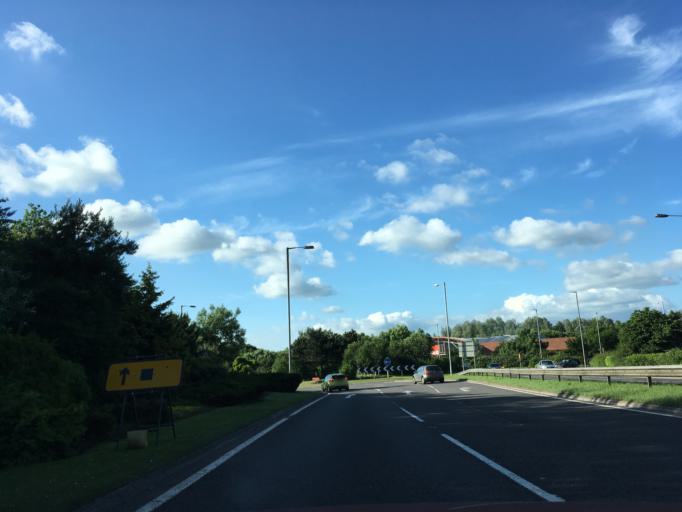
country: GB
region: England
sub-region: Somerset
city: Creech Saint Michael
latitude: 51.0212
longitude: -3.0656
